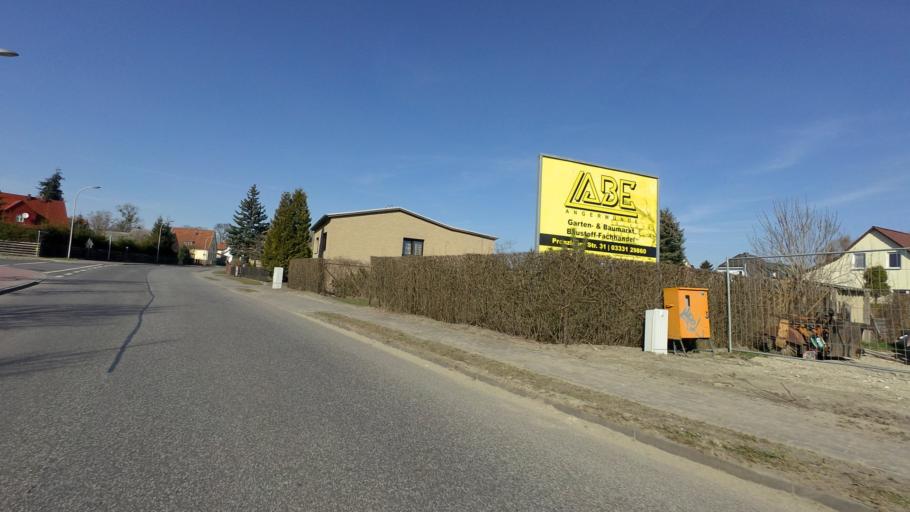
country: DE
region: Brandenburg
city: Angermunde
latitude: 53.0117
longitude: 14.0004
